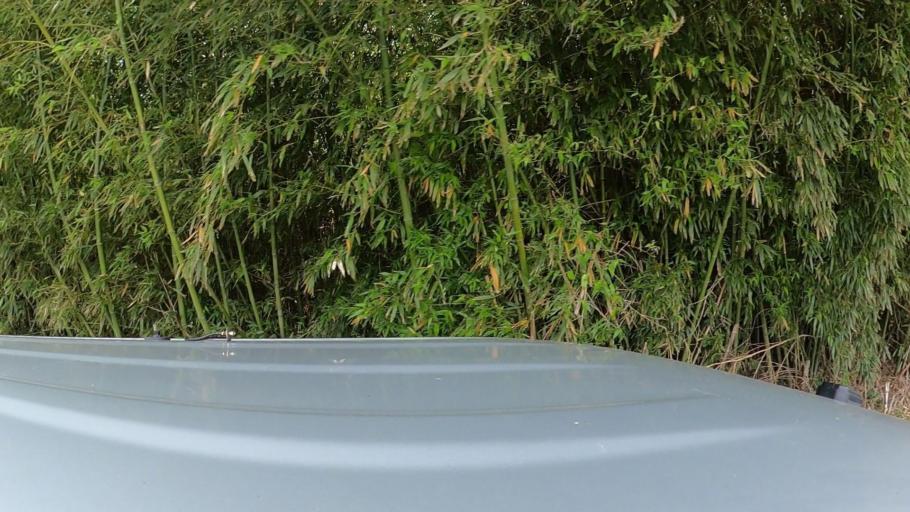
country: JP
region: Kanagawa
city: Chigasaki
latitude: 35.3490
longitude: 139.3722
